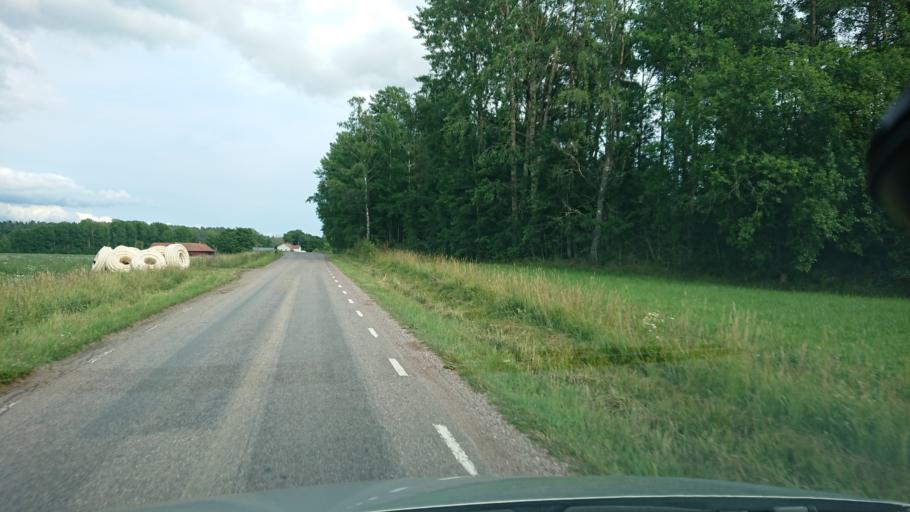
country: SE
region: Uppsala
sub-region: Osthammars Kommun
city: Bjorklinge
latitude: 59.9864
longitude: 17.5521
